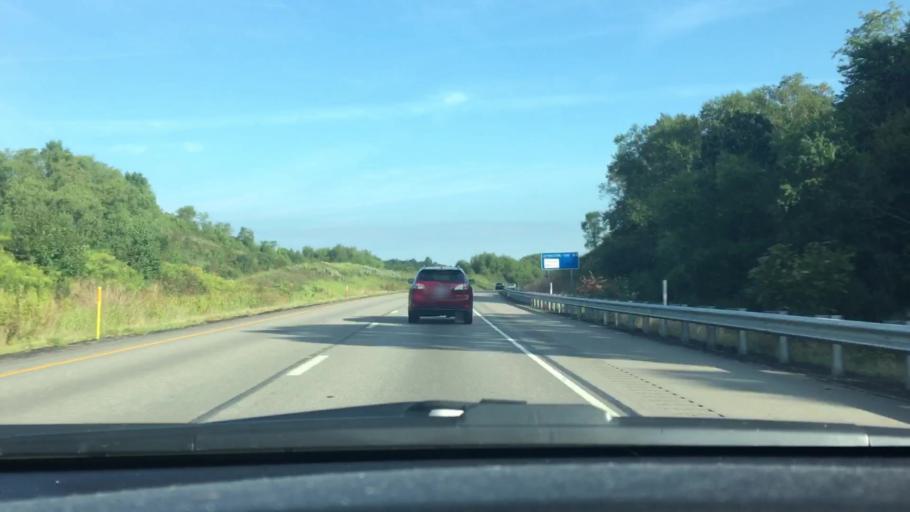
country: US
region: Pennsylvania
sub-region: Butler County
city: Fox Run
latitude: 40.7386
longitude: -80.1060
